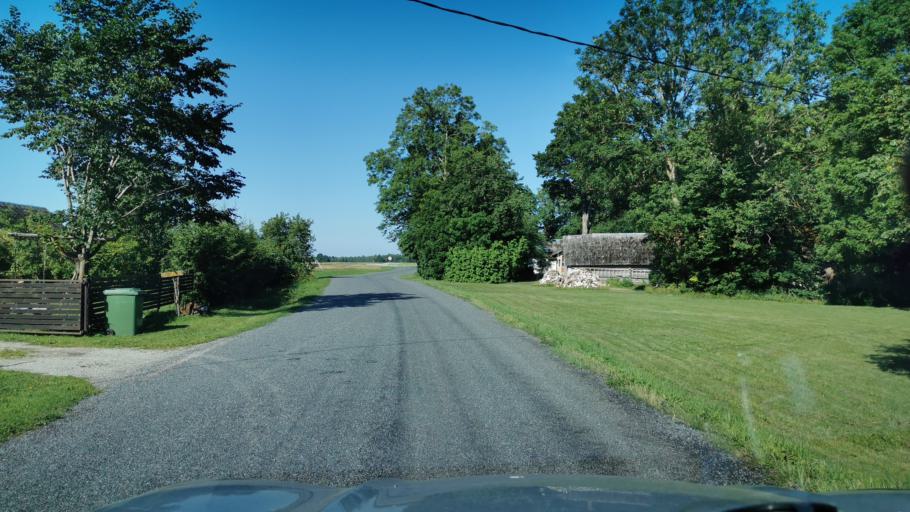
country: EE
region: Harju
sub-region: Paldiski linn
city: Paldiski
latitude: 59.2081
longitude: 24.0081
